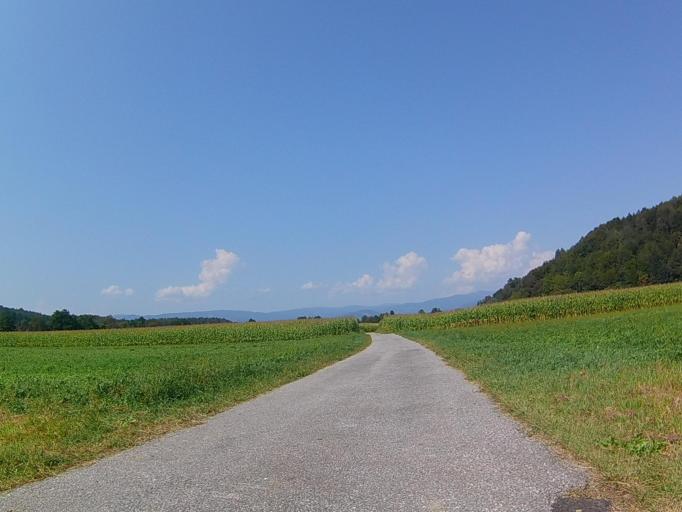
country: AT
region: Styria
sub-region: Politischer Bezirk Leibnitz
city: Oberhaag
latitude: 46.6958
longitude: 15.3213
